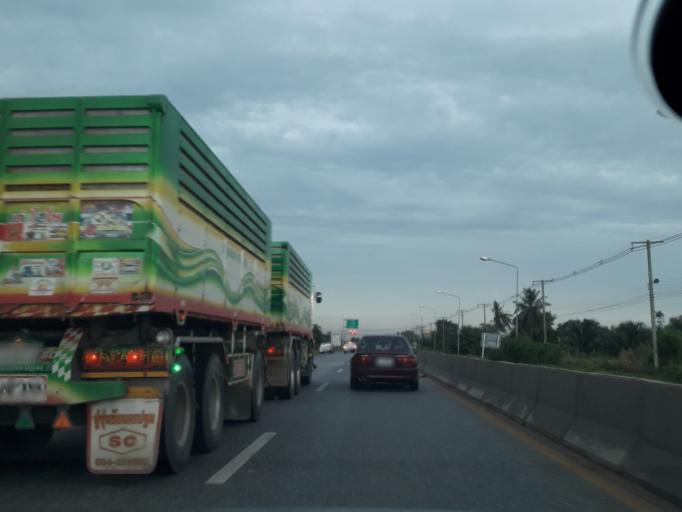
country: TH
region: Pathum Thani
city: Nong Suea
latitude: 14.1346
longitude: 100.7474
